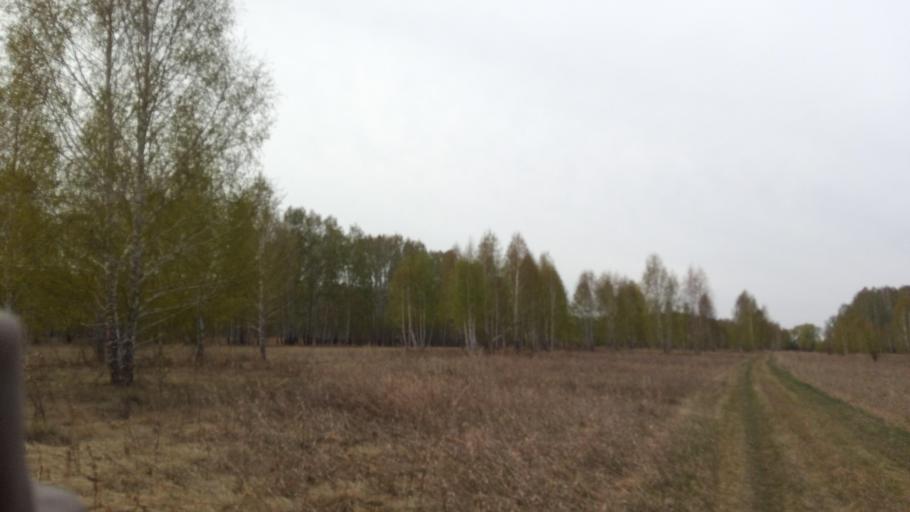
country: RU
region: Chelyabinsk
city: Timiryazevskiy
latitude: 55.0043
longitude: 60.8538
